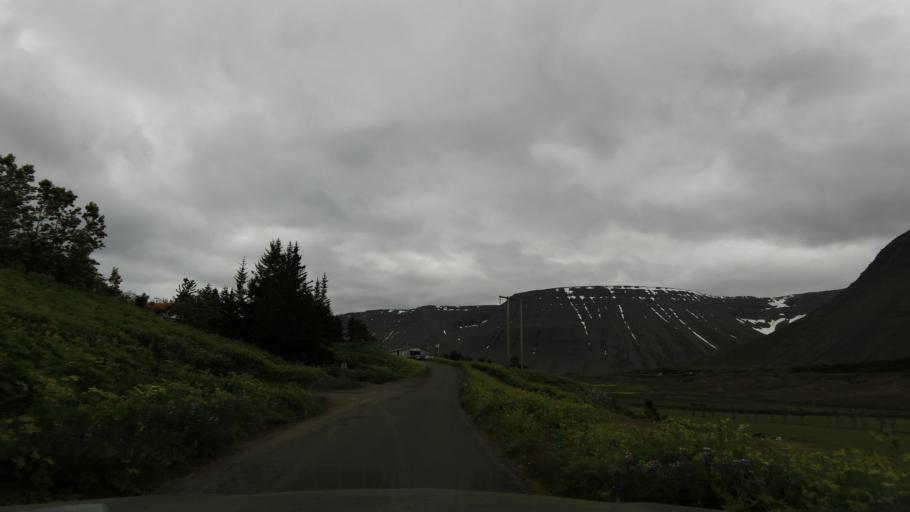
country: IS
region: Westfjords
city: Isafjoerdur
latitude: 66.0608
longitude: -23.1965
